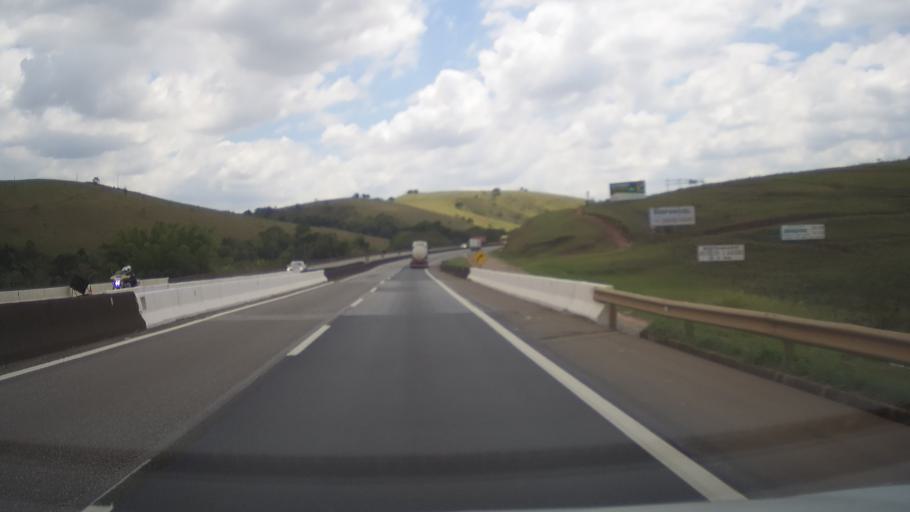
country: BR
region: Minas Gerais
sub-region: Tres Coracoes
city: Tres Coracoes
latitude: -21.7115
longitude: -45.3757
